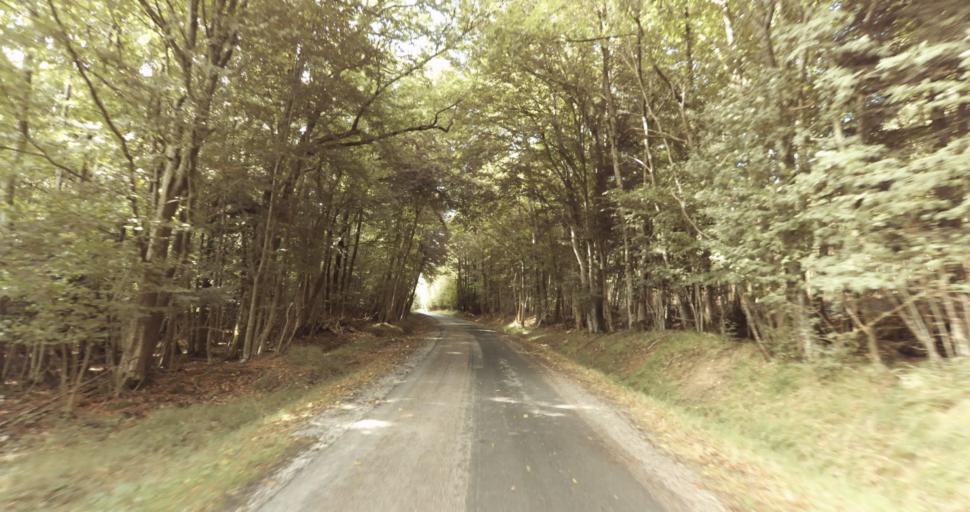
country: FR
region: Lower Normandy
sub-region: Departement de l'Orne
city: Gace
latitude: 48.7824
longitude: 0.3278
